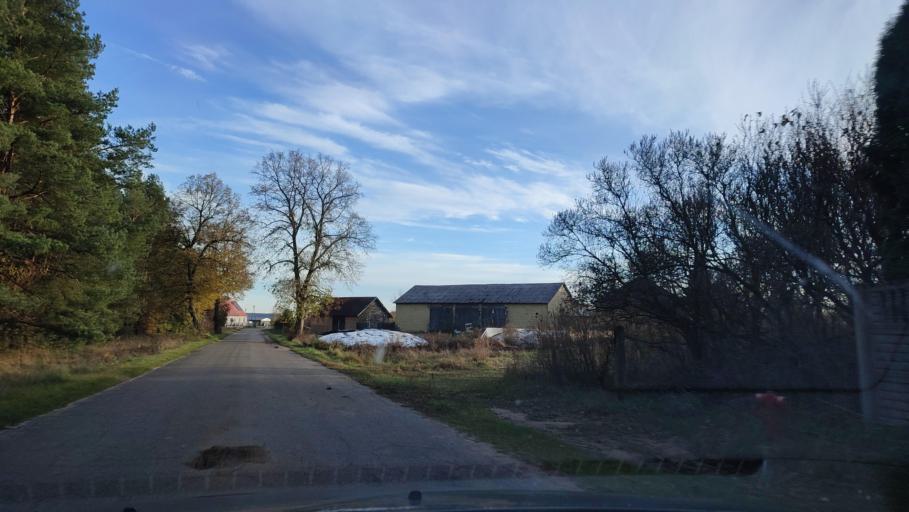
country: PL
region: Masovian Voivodeship
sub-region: Powiat przasnyski
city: Chorzele
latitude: 53.3424
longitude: 20.7528
